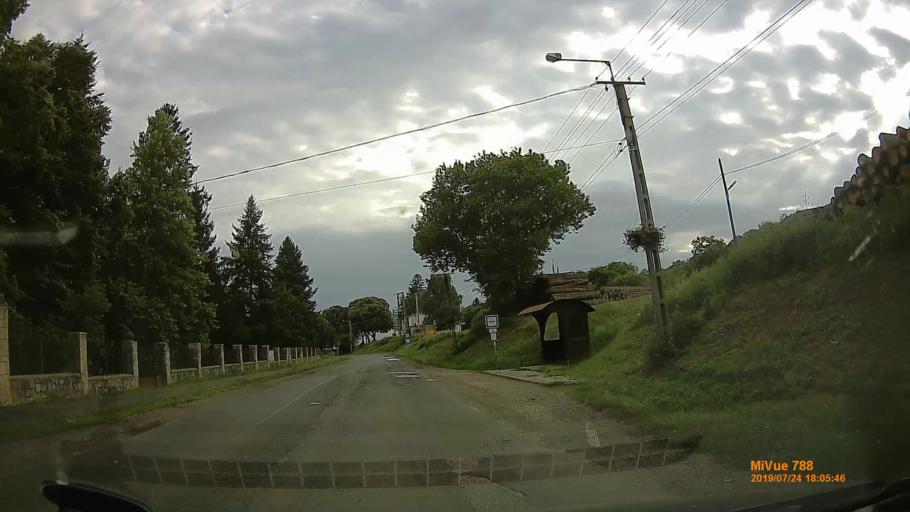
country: HU
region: Borsod-Abauj-Zemplen
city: Abaujszanto
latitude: 48.2875
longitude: 21.1831
